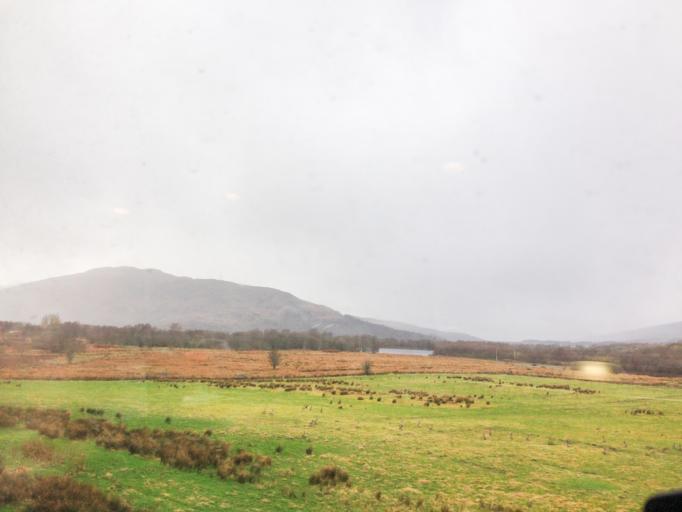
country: GB
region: Scotland
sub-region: Highland
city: Fort William
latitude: 56.8295
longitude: -5.0861
